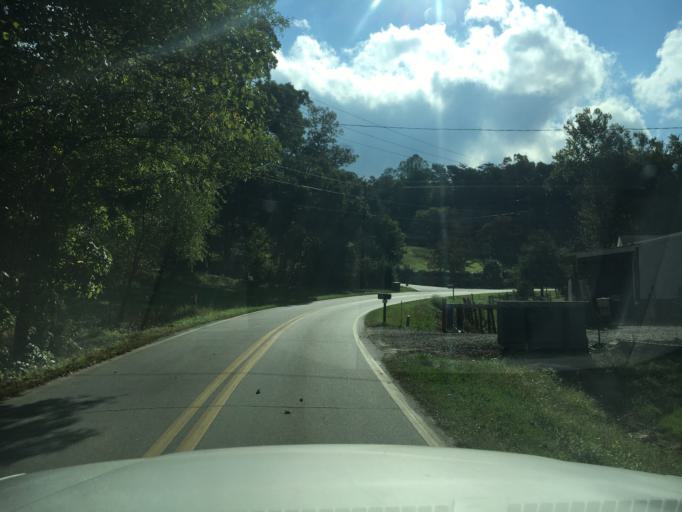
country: US
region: North Carolina
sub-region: Buncombe County
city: Swannanoa
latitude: 35.6044
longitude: -82.4304
